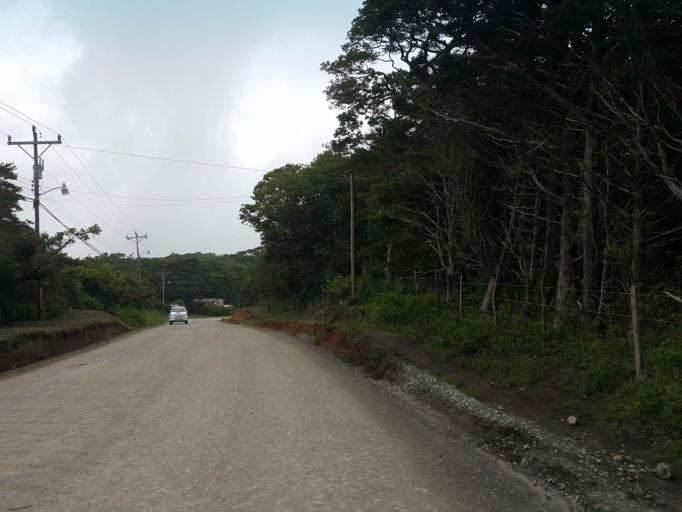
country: CR
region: Guanacaste
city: Juntas
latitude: 10.3082
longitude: -84.8299
